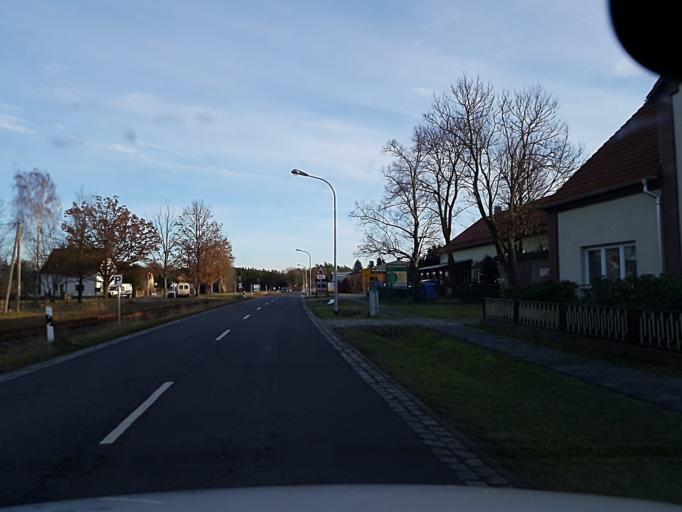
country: DE
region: Brandenburg
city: Finsterwalde
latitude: 51.6140
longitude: 13.7587
